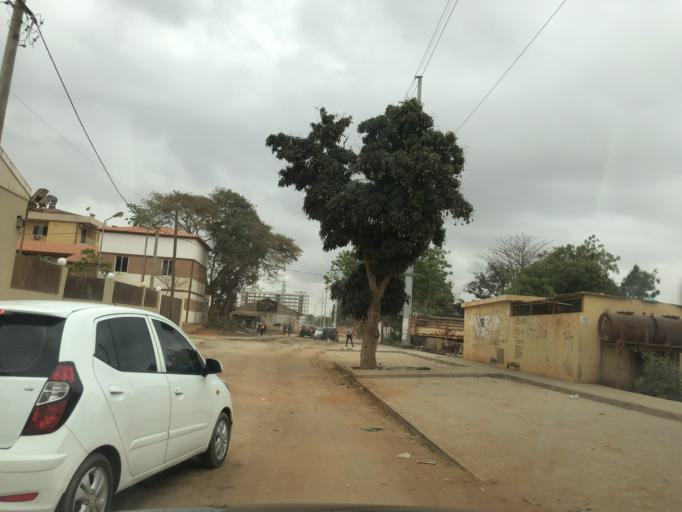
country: AO
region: Luanda
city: Luanda
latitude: -8.8990
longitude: 13.1970
